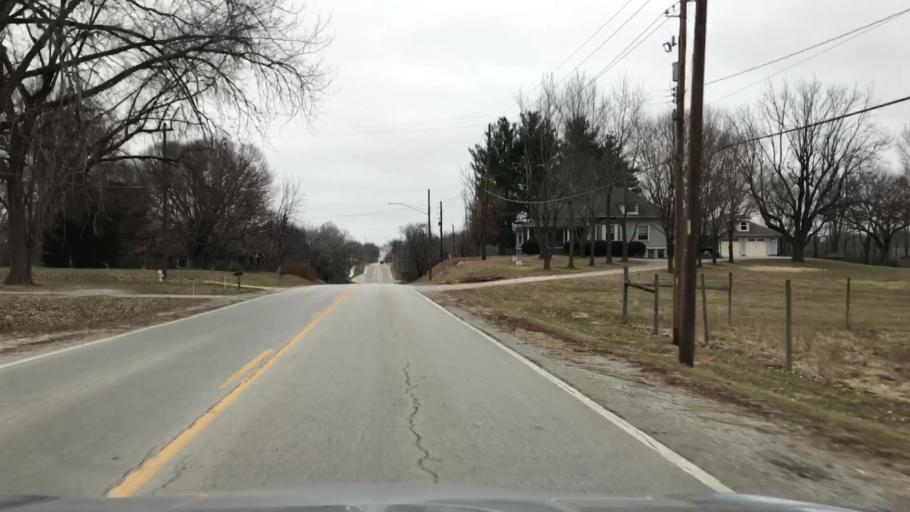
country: US
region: Missouri
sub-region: Clay County
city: Liberty
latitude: 39.2553
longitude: -94.4167
